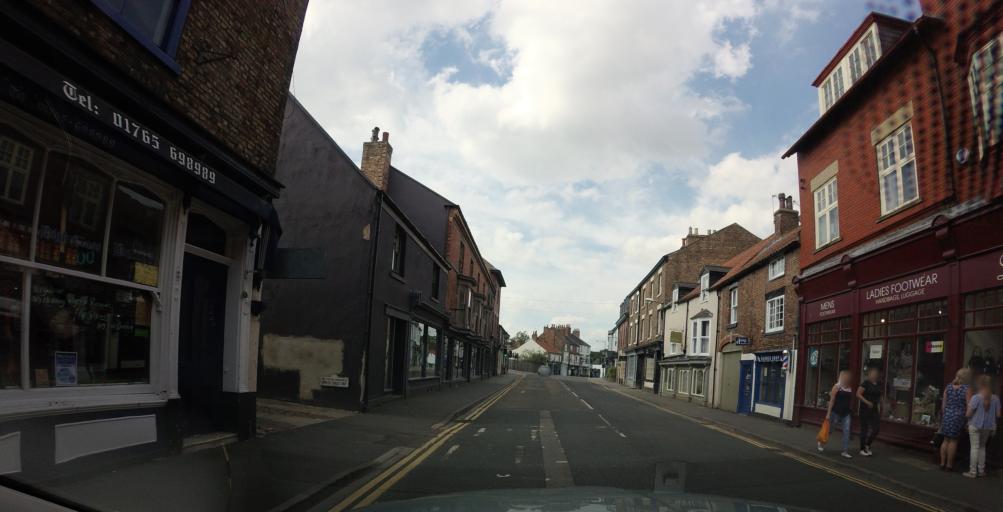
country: GB
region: England
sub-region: North Yorkshire
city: Ripon
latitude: 54.1382
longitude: -1.5239
